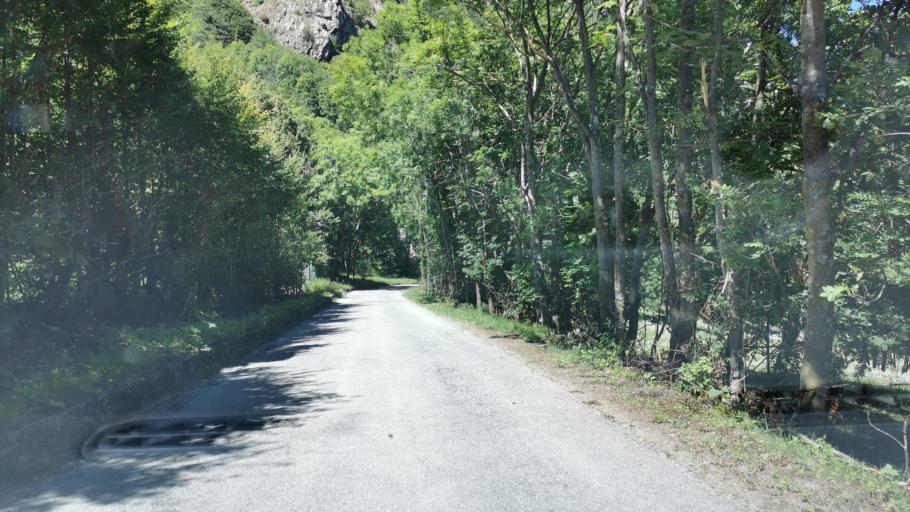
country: IT
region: Piedmont
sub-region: Provincia di Cuneo
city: Entracque
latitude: 44.2106
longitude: 7.3816
